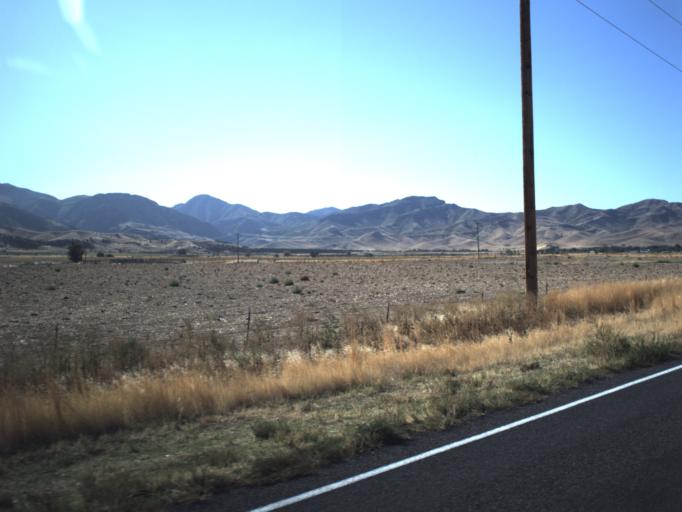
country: US
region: Utah
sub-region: Millard County
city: Delta
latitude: 39.4043
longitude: -112.3338
